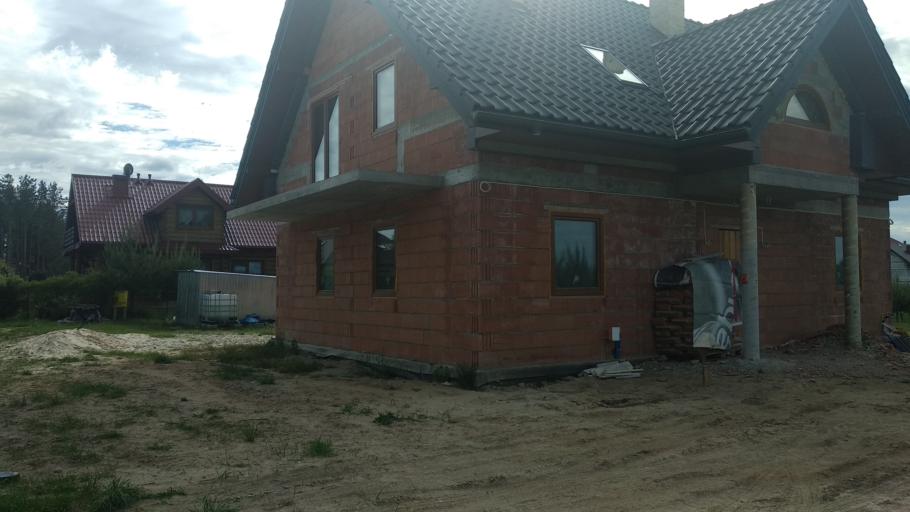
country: PL
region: Swietokrzyskie
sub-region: Powiat kielecki
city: Checiny
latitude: 50.8192
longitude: 20.4111
